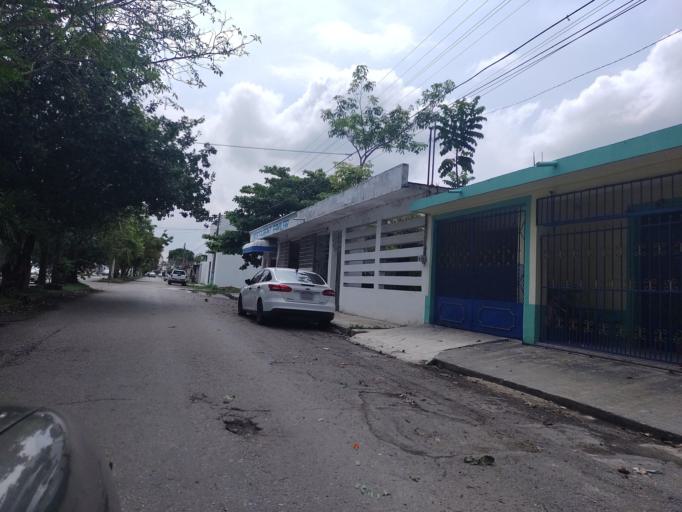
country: MX
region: Quintana Roo
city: Chetumal
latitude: 18.5169
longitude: -88.3121
